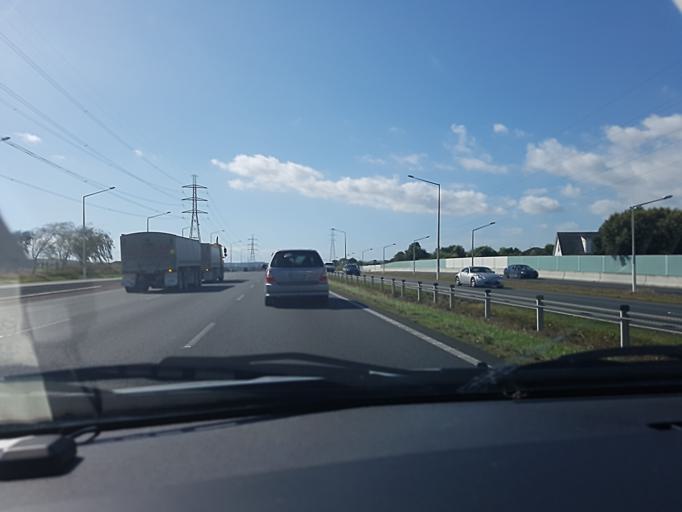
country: NZ
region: Auckland
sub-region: Auckland
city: Papakura
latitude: -37.0700
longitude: 174.9276
